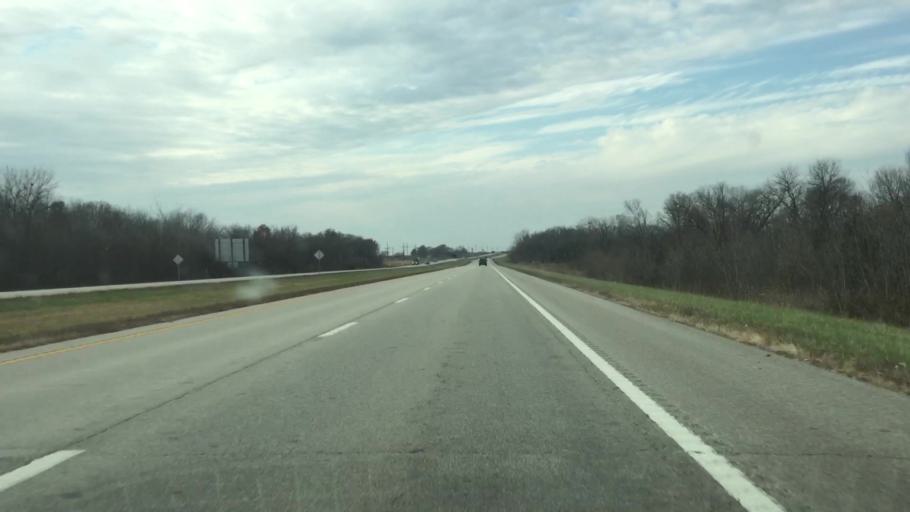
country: US
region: Missouri
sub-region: Cass County
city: Garden City
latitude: 38.5797
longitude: -94.2131
